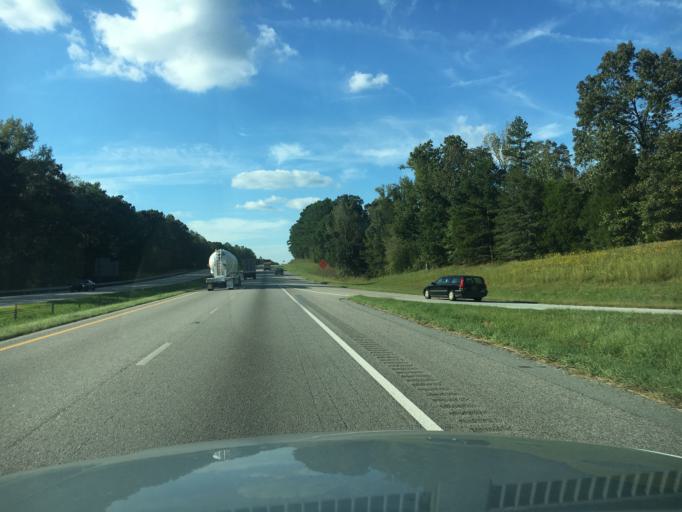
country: US
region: South Carolina
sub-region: Laurens County
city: Watts Mills
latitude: 34.6185
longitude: -81.9020
